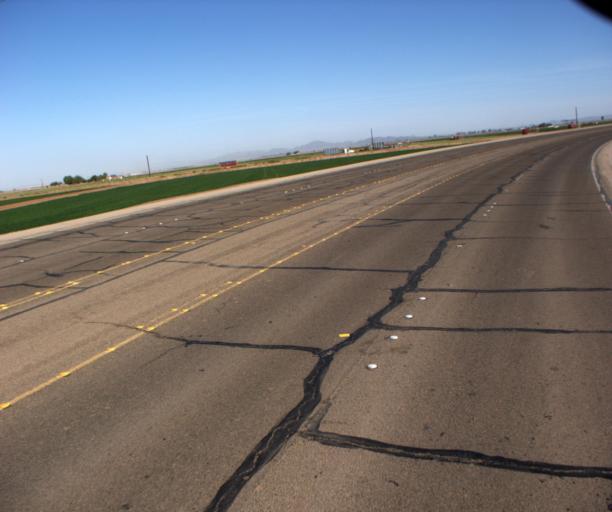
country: US
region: Arizona
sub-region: Yuma County
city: San Luis
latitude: 32.5651
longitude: -114.7843
